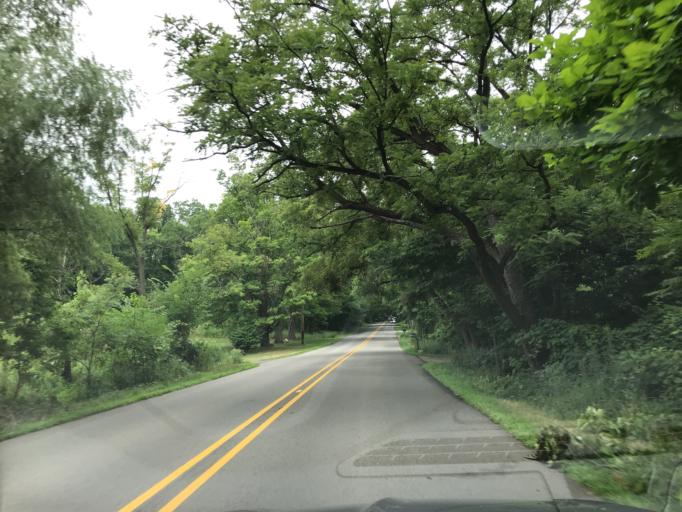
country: US
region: Michigan
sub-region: Eaton County
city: Waverly
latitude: 42.7597
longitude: -84.6547
